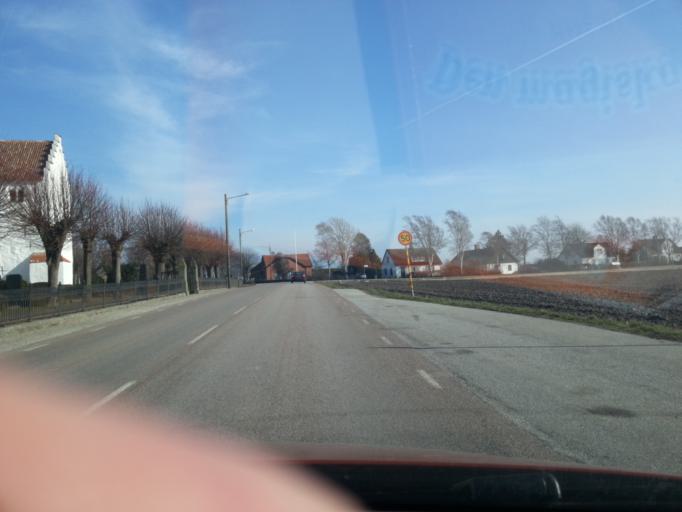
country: SE
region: Skane
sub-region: Ystads Kommun
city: Kopingebro
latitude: 55.4284
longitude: 14.0615
